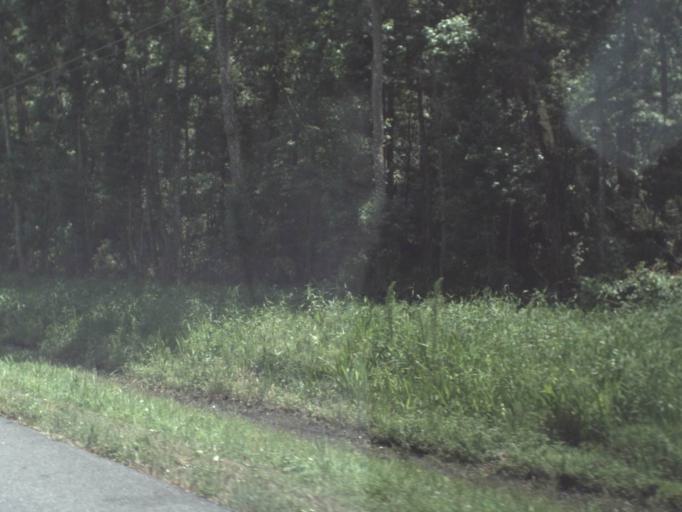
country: US
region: Florida
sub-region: Putnam County
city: Palatka
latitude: 29.6964
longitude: -81.7603
